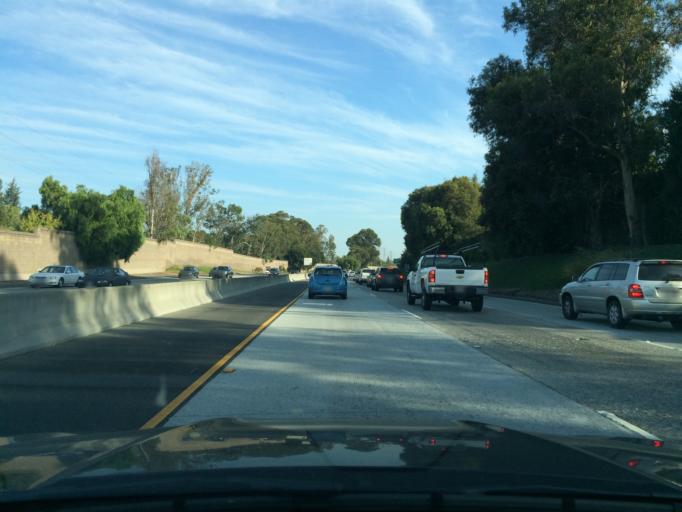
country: US
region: California
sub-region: Santa Clara County
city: Mountain View
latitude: 37.3674
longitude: -122.0642
